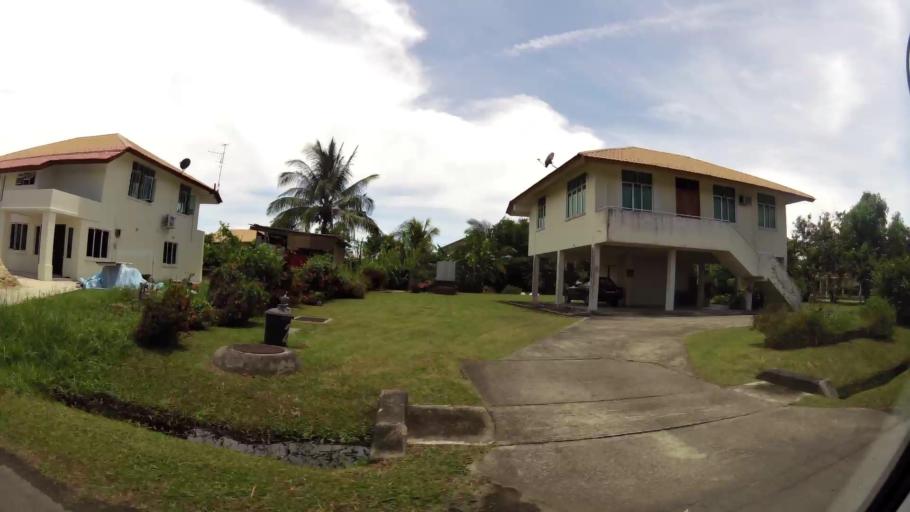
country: BN
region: Belait
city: Kuala Belait
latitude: 4.5881
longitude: 114.2467
